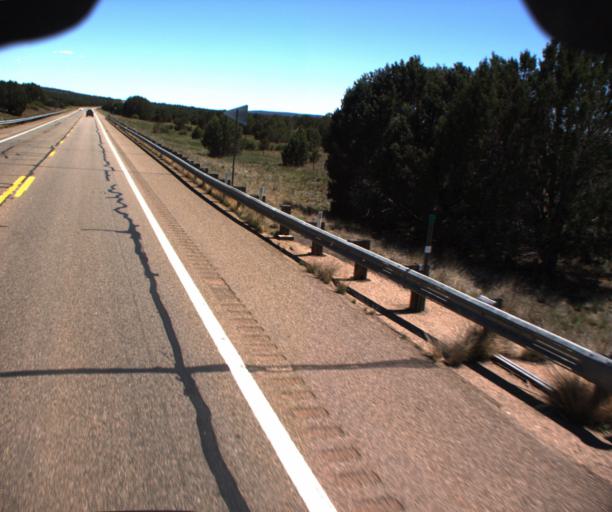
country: US
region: Arizona
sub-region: Yavapai County
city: Paulden
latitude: 35.1301
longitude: -112.4383
